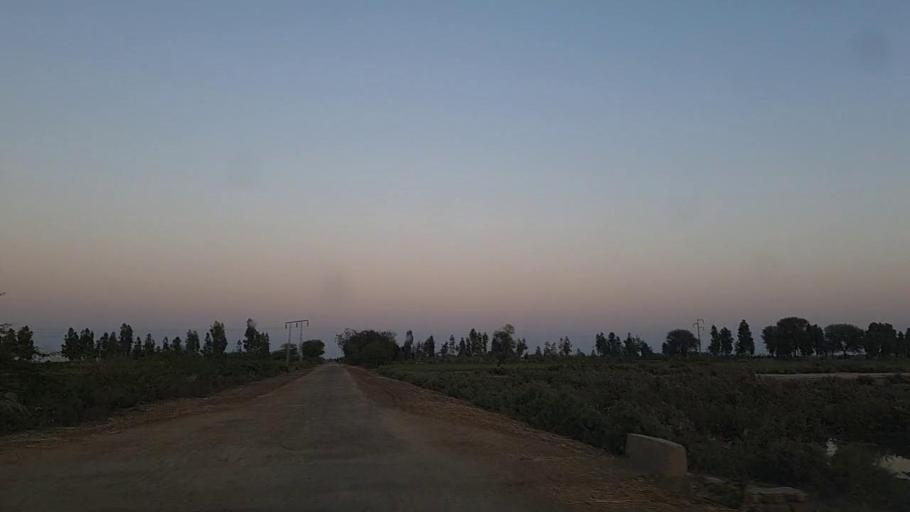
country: PK
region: Sindh
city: Samaro
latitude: 25.3252
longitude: 69.3910
